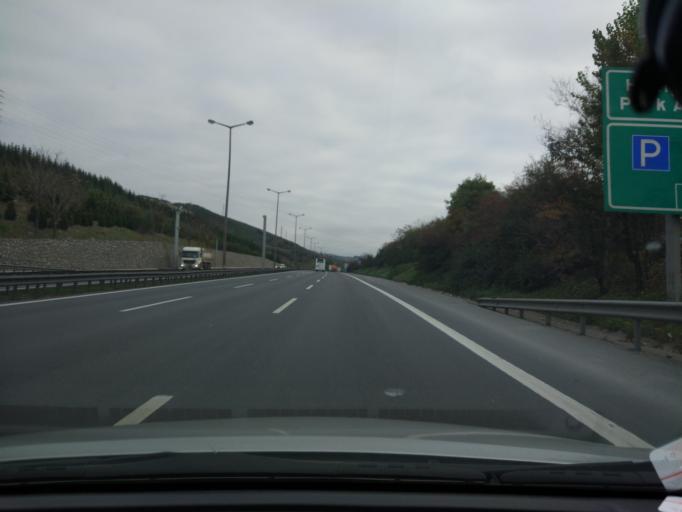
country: TR
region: Kocaeli
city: Izmit
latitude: 40.7691
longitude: 29.8680
